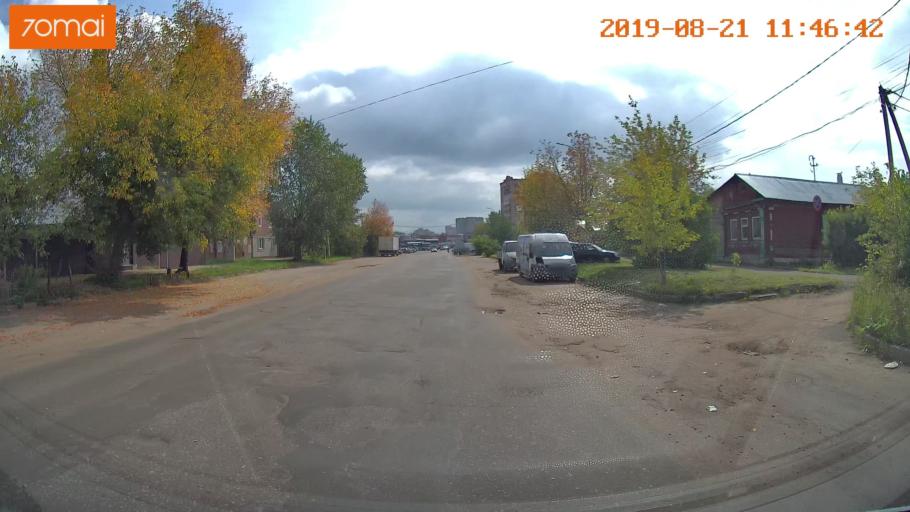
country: RU
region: Ivanovo
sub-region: Gorod Ivanovo
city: Ivanovo
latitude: 56.9911
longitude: 40.9646
